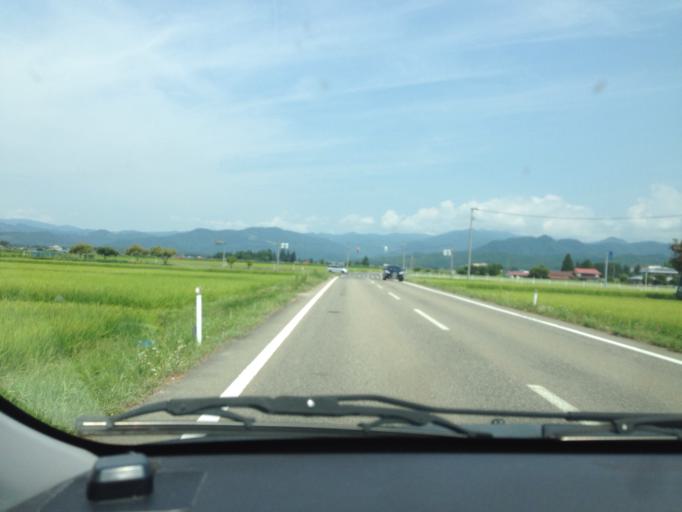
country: JP
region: Fukushima
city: Kitakata
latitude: 37.6642
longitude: 139.8808
